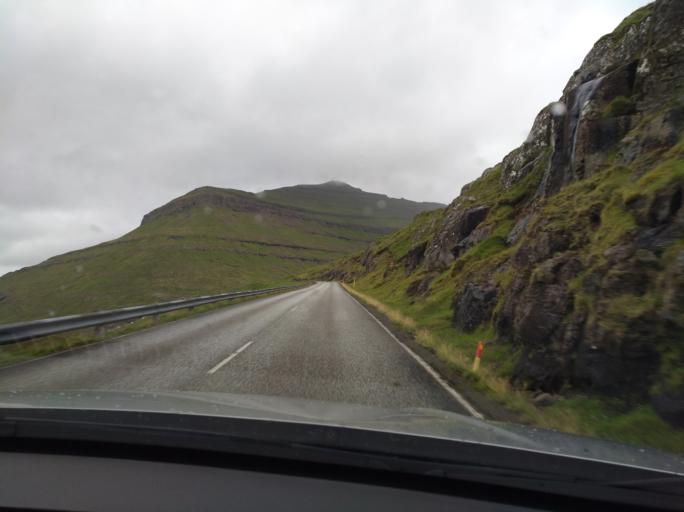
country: FO
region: Eysturoy
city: Fuglafjordur
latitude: 62.2200
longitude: -6.8701
